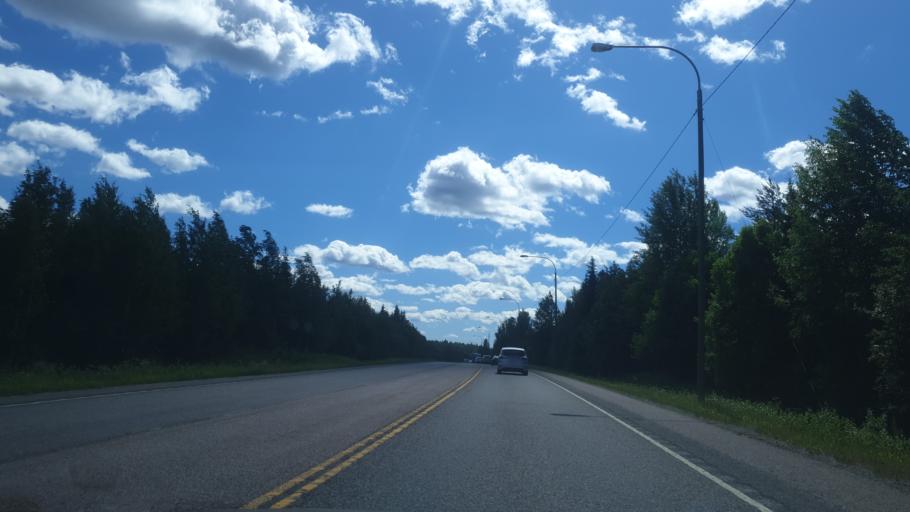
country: FI
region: Northern Savo
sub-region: Varkaus
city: Varkaus
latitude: 62.3597
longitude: 27.8109
